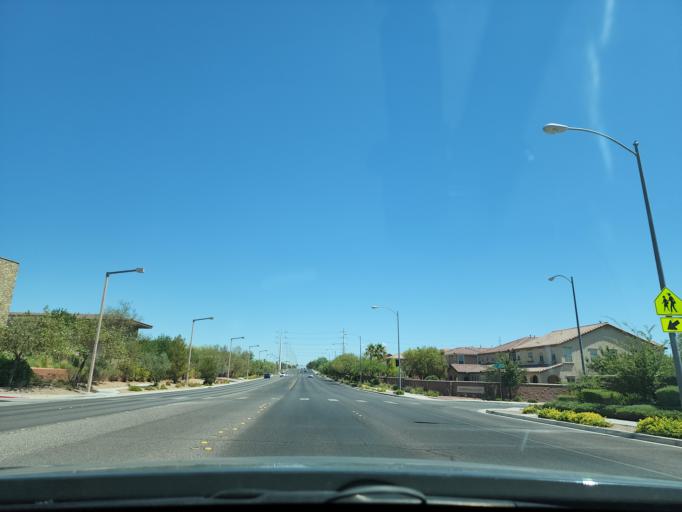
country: US
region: Nevada
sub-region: Clark County
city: Summerlin South
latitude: 36.0812
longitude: -115.3155
